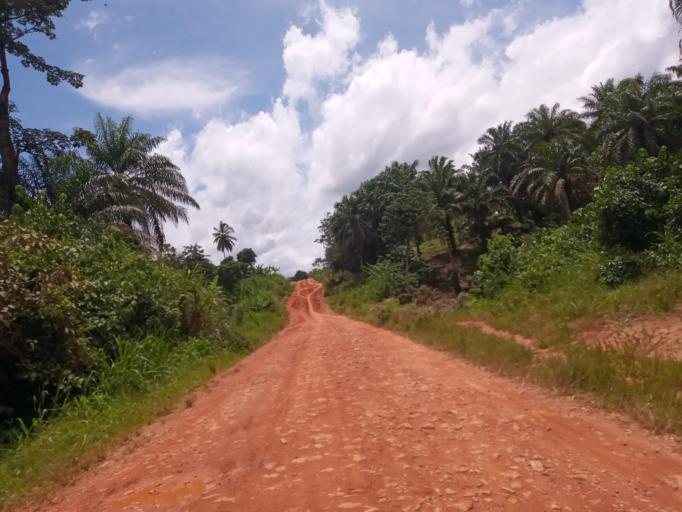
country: SL
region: Eastern Province
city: Koidu
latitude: 8.6440
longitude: -10.9111
